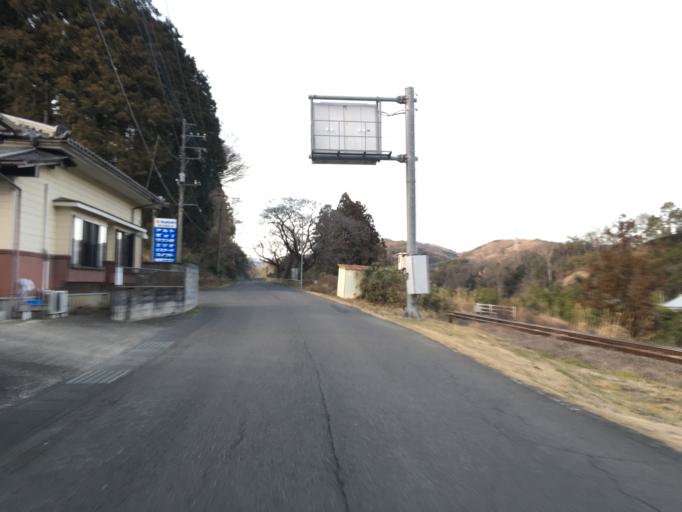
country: JP
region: Ibaraki
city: Daigo
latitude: 36.8096
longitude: 140.3704
